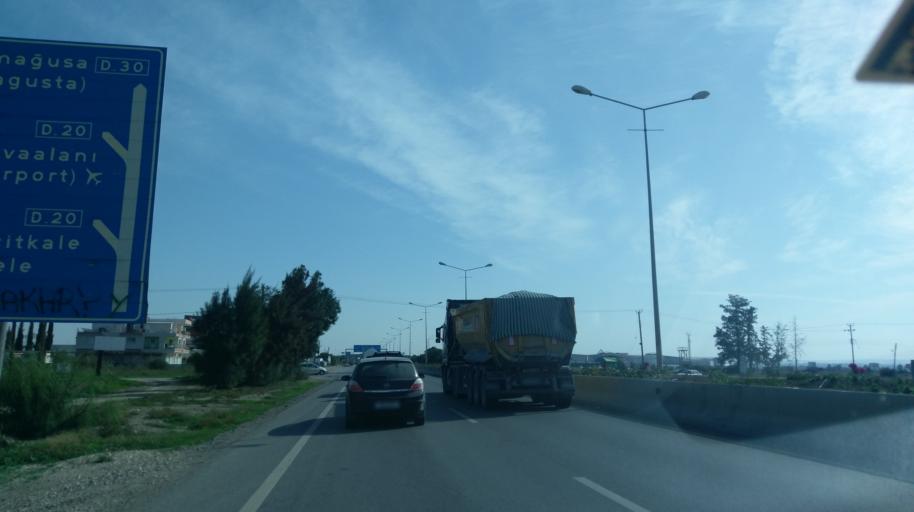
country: CY
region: Lefkosia
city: Nicosia
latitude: 35.2207
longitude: 33.4908
